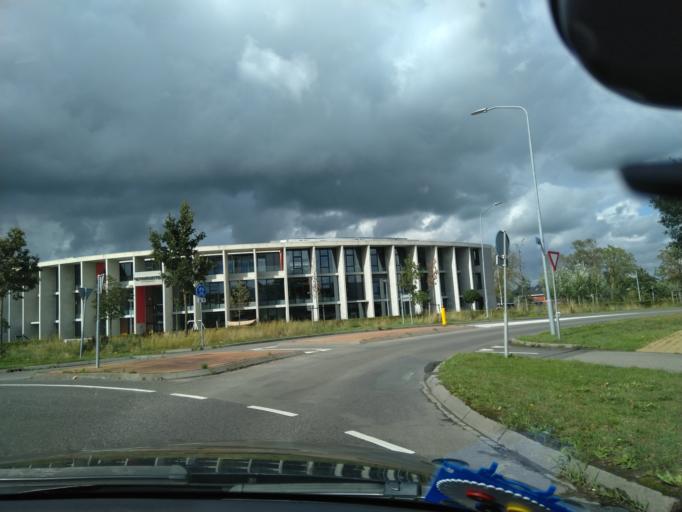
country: NL
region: Groningen
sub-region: Gemeente Zuidhorn
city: Zuidhorn
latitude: 53.2495
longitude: 6.4076
